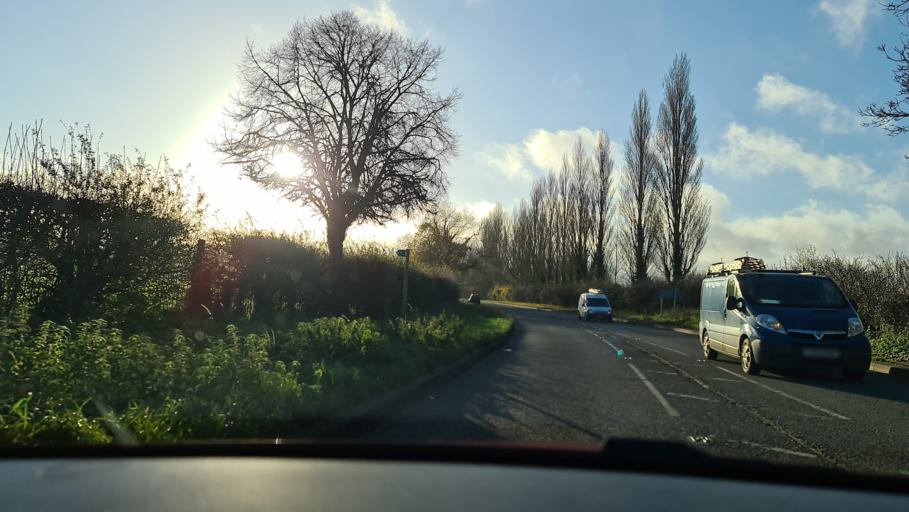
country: GB
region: England
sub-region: Buckinghamshire
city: Weston Turville
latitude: 51.7699
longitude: -0.7887
